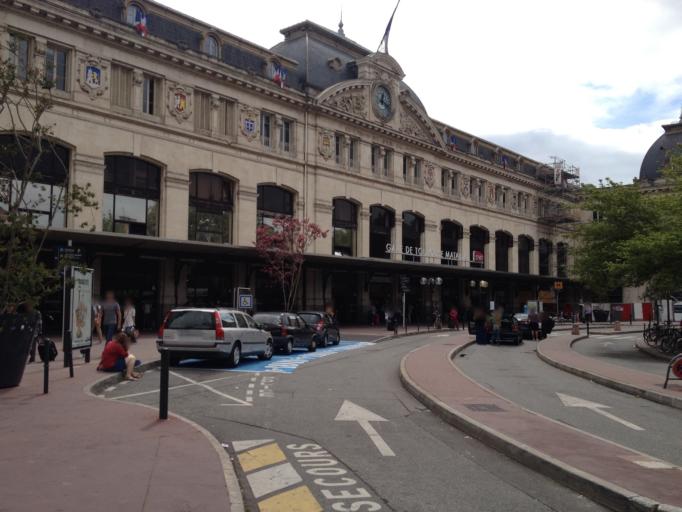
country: FR
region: Midi-Pyrenees
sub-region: Departement de la Haute-Garonne
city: Toulouse
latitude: 43.6115
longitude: 1.4530
